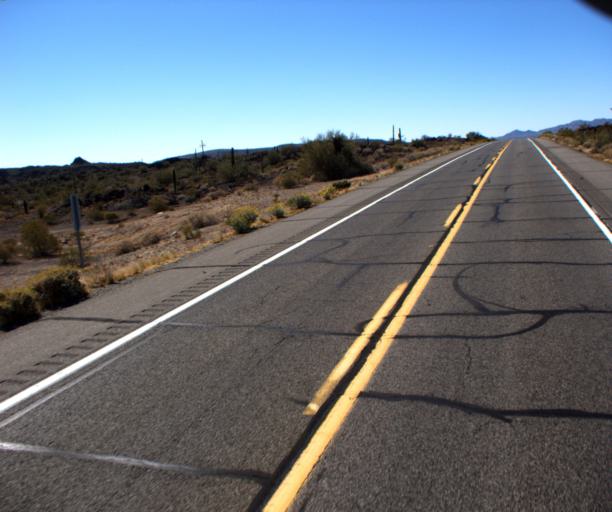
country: US
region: Arizona
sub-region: Pima County
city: Ajo
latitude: 32.5423
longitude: -112.8800
